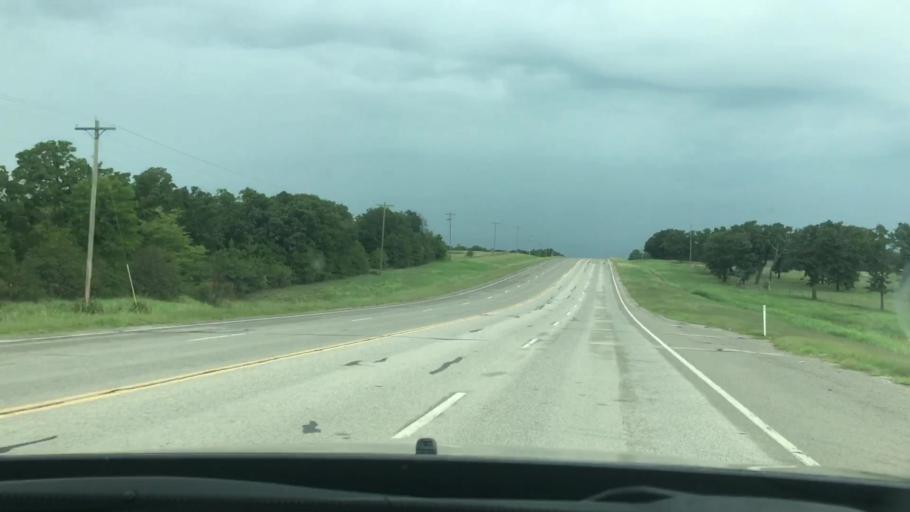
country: US
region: Oklahoma
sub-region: Carter County
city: Healdton
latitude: 34.1894
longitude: -97.4747
